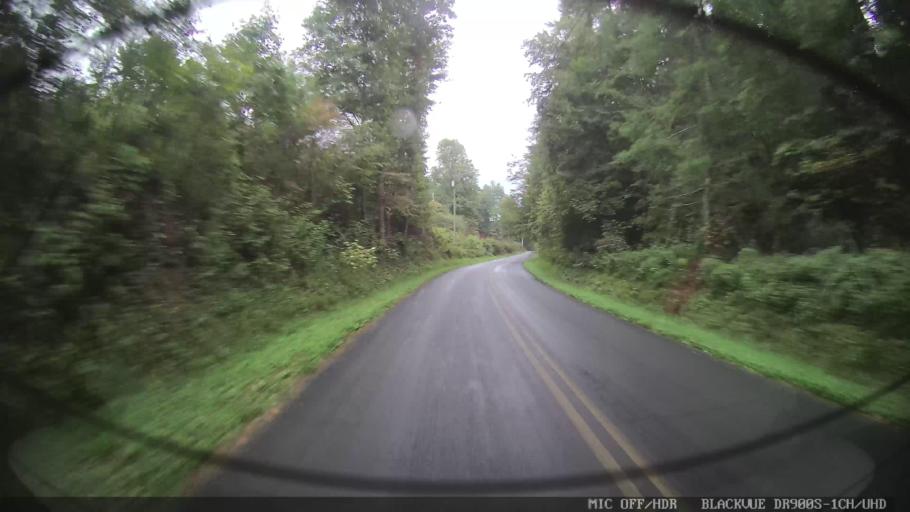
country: US
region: Georgia
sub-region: Gilmer County
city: Ellijay
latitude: 34.7823
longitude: -84.5455
